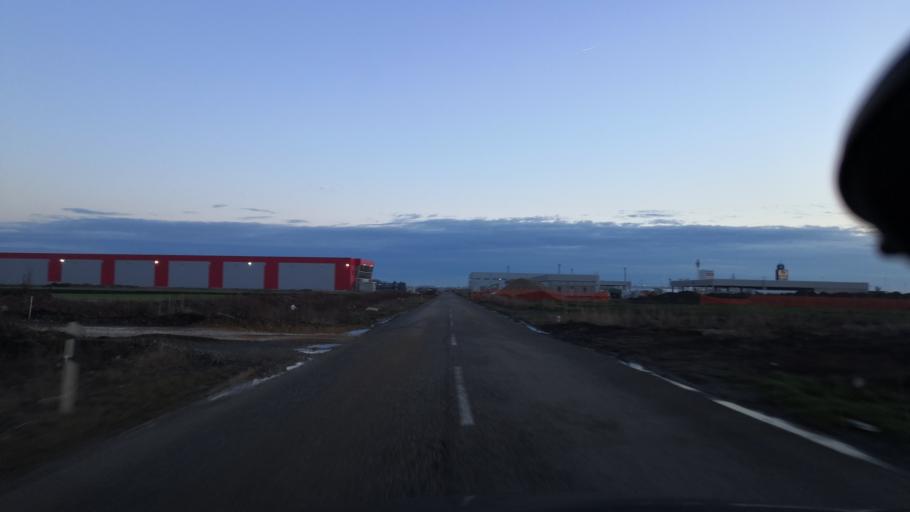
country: RS
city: Simanovci
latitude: 44.8883
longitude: 20.1107
